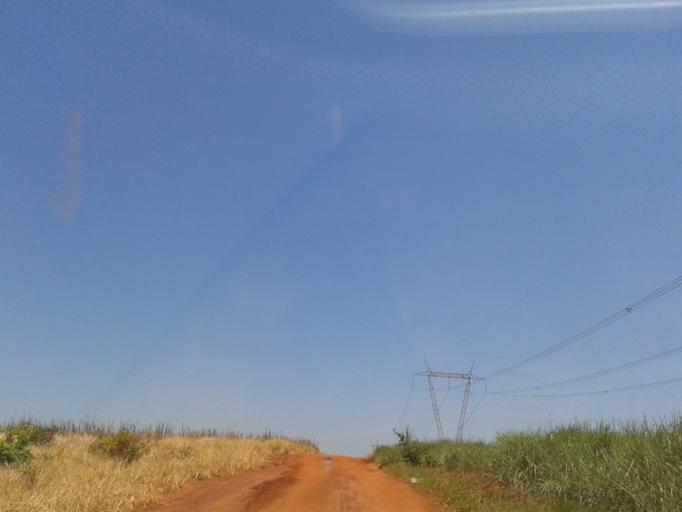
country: BR
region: Minas Gerais
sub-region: Santa Vitoria
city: Santa Vitoria
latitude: -19.0865
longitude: -50.4534
